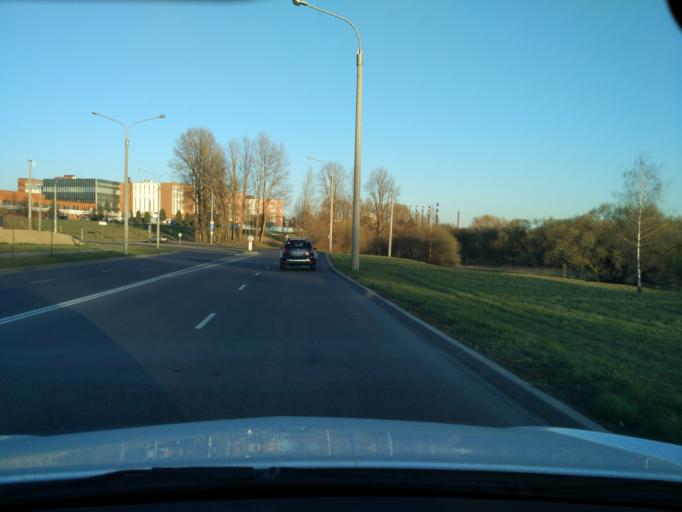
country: BY
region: Minsk
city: Syenitsa
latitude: 53.8643
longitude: 27.5000
